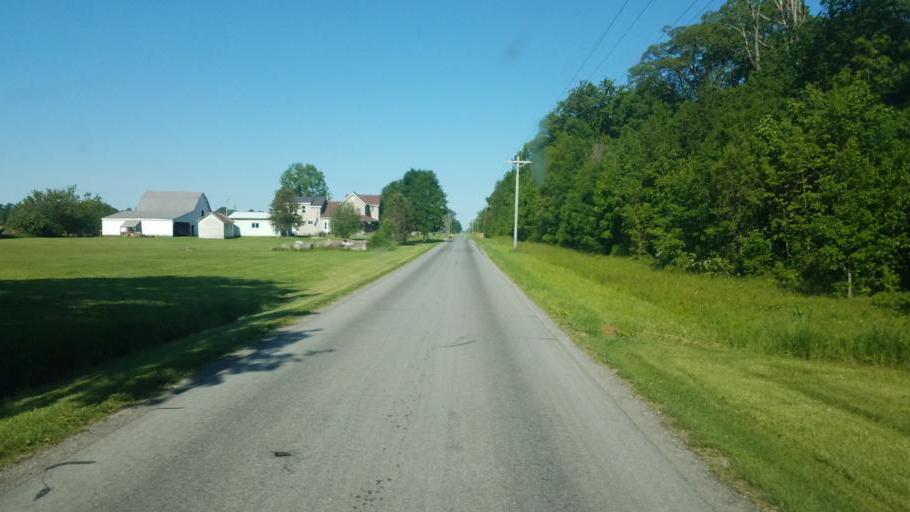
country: US
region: Ohio
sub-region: Hardin County
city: Kenton
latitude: 40.5798
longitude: -83.5617
